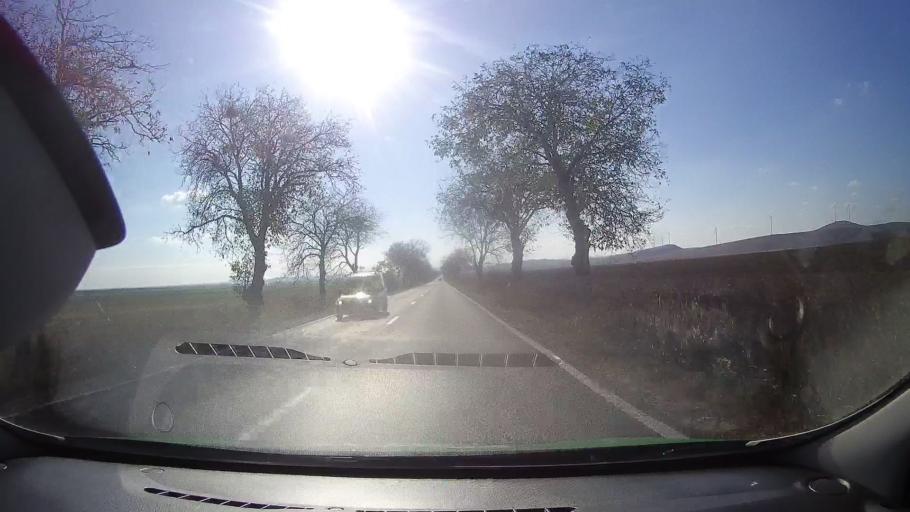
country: RO
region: Tulcea
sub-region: Comuna Ceamurlia de Jos
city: Ceamurlia de Jos
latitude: 44.7997
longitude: 28.6905
